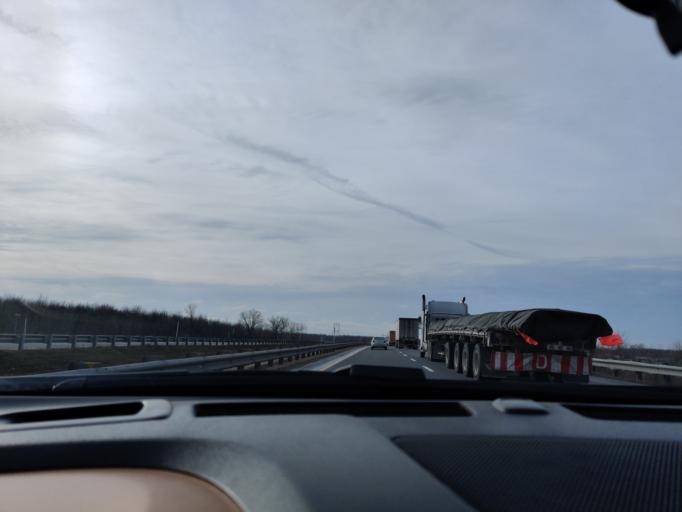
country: CA
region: Quebec
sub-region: Monteregie
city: Les Coteaux
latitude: 45.2716
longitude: -74.2158
